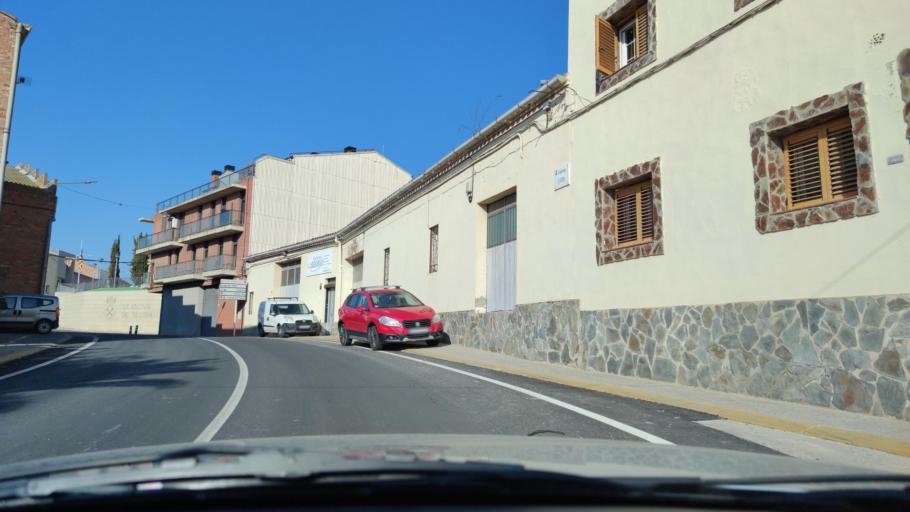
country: ES
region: Catalonia
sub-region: Provincia de Lleida
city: Torrefarrera
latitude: 41.7111
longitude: 0.6212
